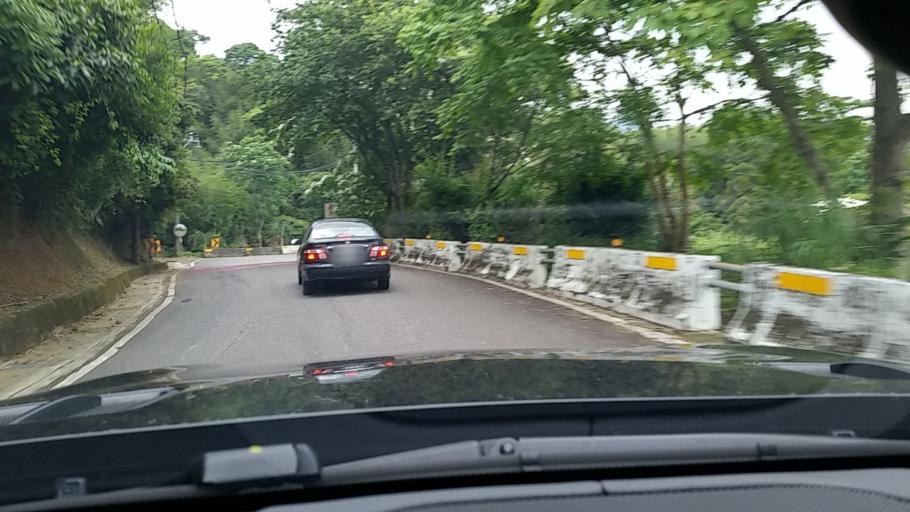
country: TW
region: Taiwan
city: Daxi
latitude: 24.7989
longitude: 121.3111
